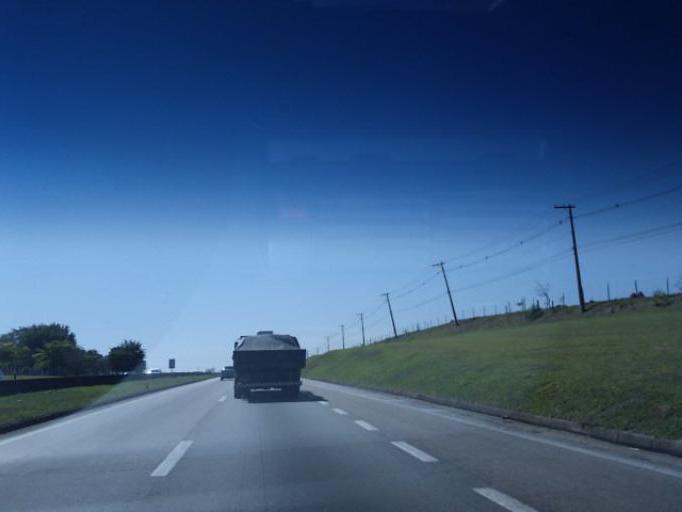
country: BR
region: Sao Paulo
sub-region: Sao Jose Dos Campos
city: Sao Jose dos Campos
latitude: -23.1601
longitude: -45.8012
